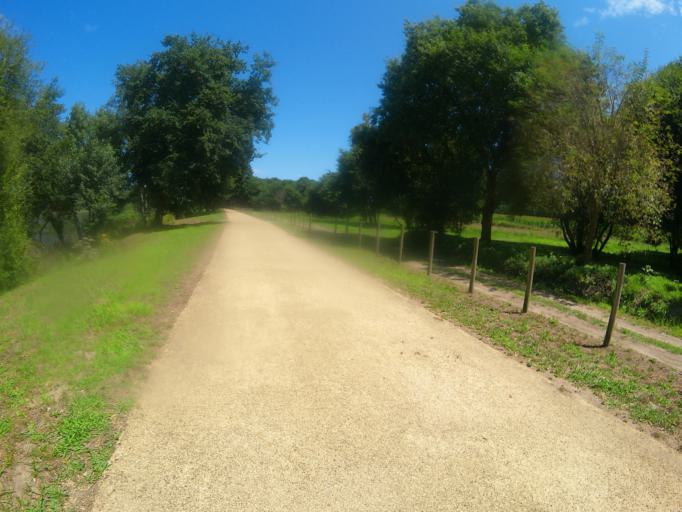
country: PT
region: Viana do Castelo
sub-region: Vila Nova de Cerveira
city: Vila Nova de Cerveira
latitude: 41.9613
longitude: -8.7439
